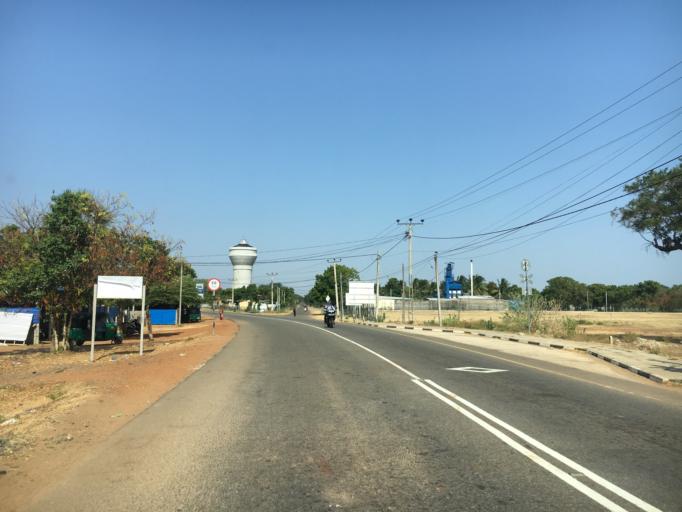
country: LK
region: Northern Province
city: Kilinochchi
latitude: 9.4380
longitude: 80.4071
